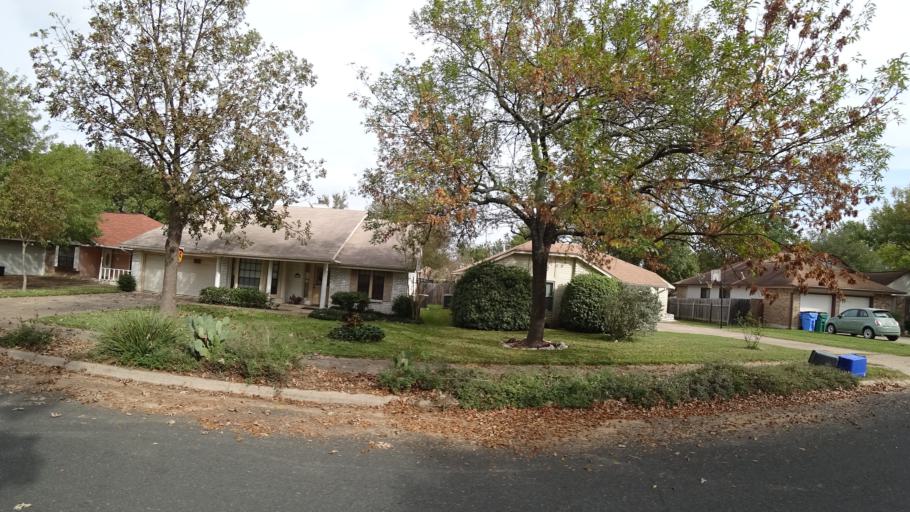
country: US
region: Texas
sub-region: Travis County
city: Wells Branch
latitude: 30.4429
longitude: -97.6827
